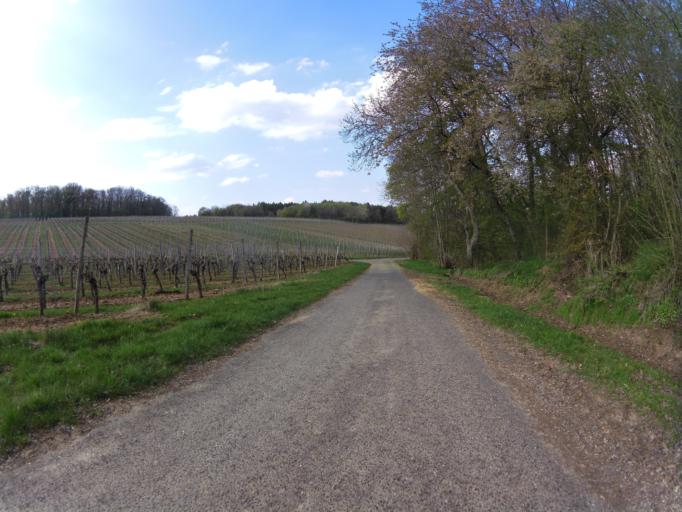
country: DE
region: Bavaria
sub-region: Regierungsbezirk Unterfranken
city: Winterhausen
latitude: 49.6945
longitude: 10.0102
